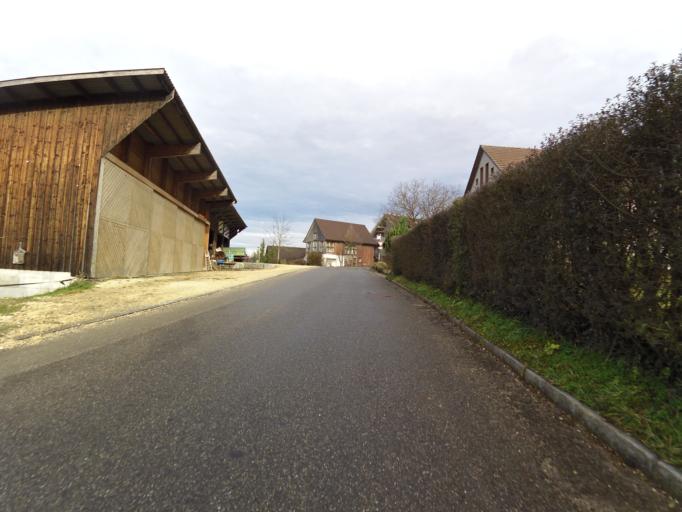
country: CH
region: Thurgau
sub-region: Frauenfeld District
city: Frauenfeld
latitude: 47.5488
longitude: 8.9215
